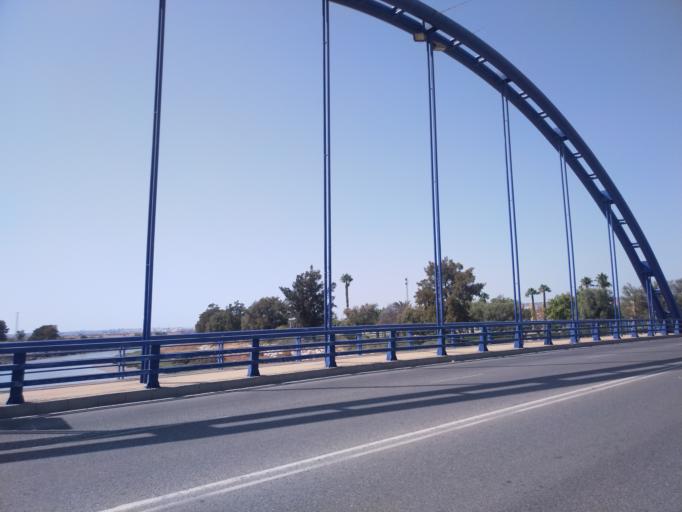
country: ES
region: Andalusia
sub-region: Provincia de Cadiz
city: Chiclana de la Frontera
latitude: 36.4239
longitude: -6.1539
